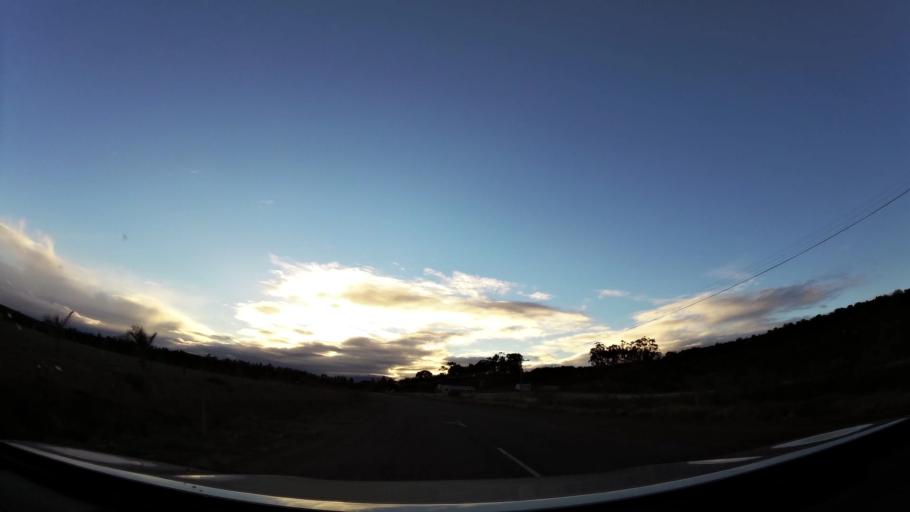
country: ZA
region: Western Cape
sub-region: Eden District Municipality
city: Riversdale
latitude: -34.0768
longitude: 20.9211
